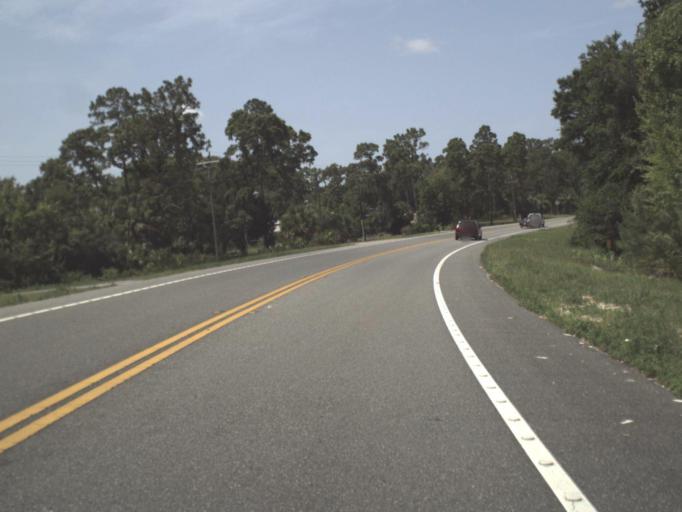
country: US
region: Florida
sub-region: Taylor County
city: Steinhatchee
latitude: 29.6905
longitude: -83.3563
